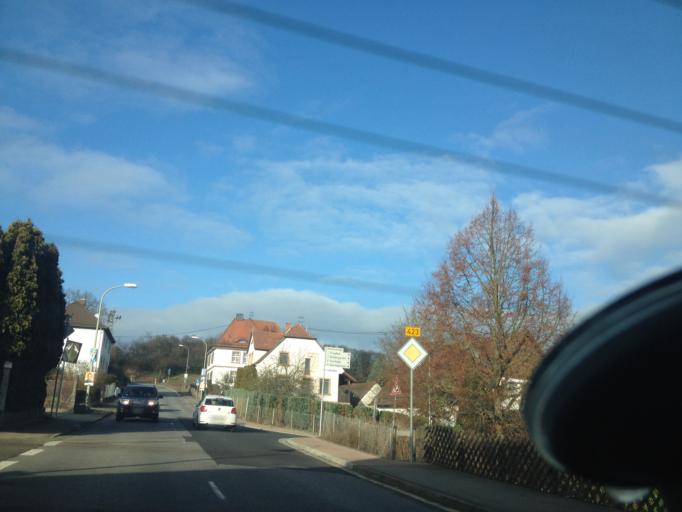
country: DE
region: Rheinland-Pfalz
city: Glan-Munchweiler
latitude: 49.4730
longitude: 7.4383
